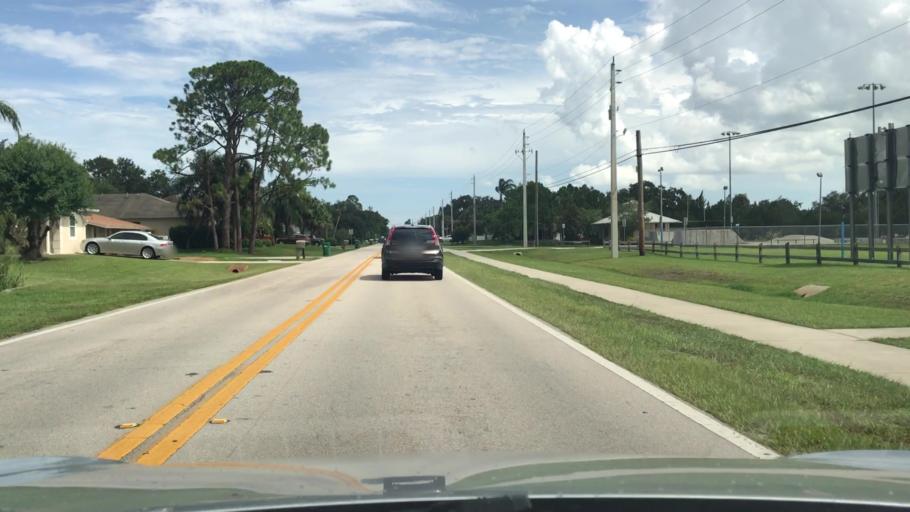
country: US
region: Florida
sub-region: Indian River County
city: Sebastian
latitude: 27.7775
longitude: -80.4860
